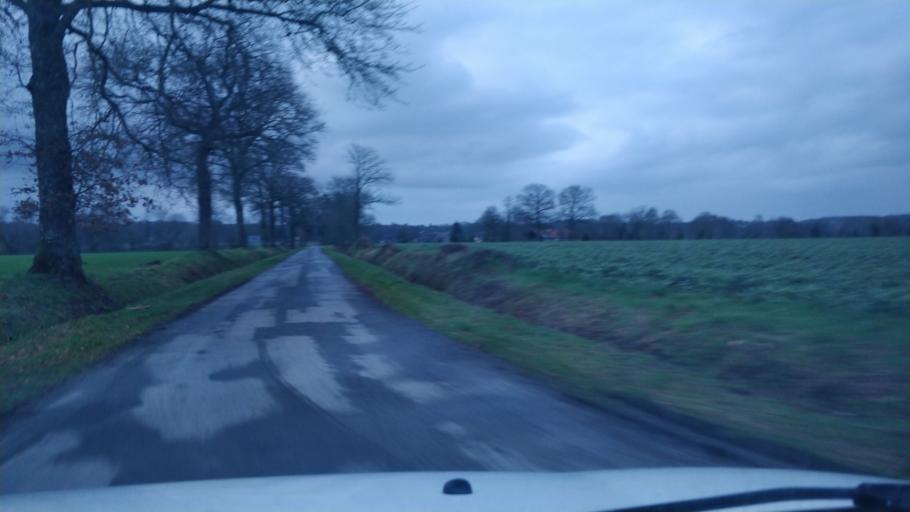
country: FR
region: Brittany
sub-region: Departement d'Ille-et-Vilaine
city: Livre-sur-Changeon
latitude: 48.1894
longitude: -1.3164
